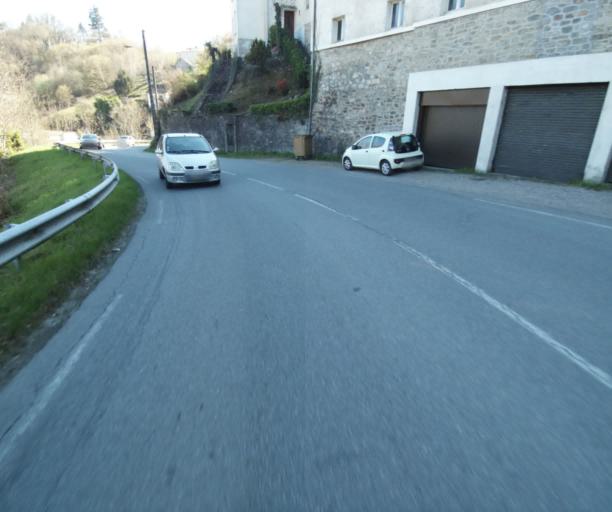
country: FR
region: Limousin
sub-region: Departement de la Correze
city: Tulle
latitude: 45.2629
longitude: 1.7442
